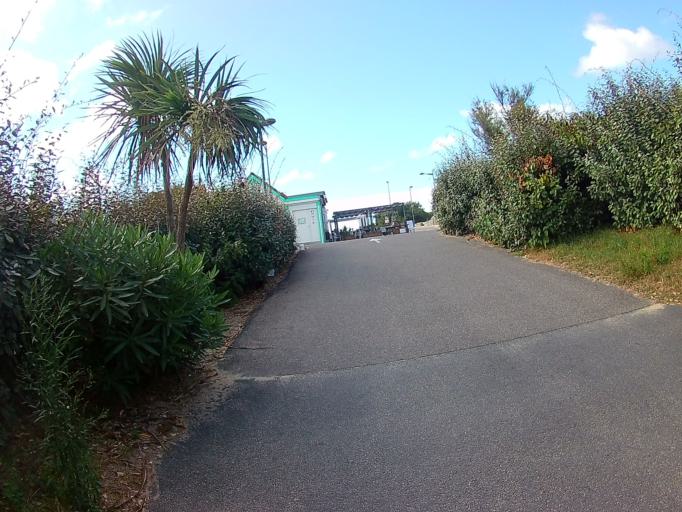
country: FR
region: Aquitaine
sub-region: Departement des Landes
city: Ondres
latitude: 43.5992
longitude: -1.4715
